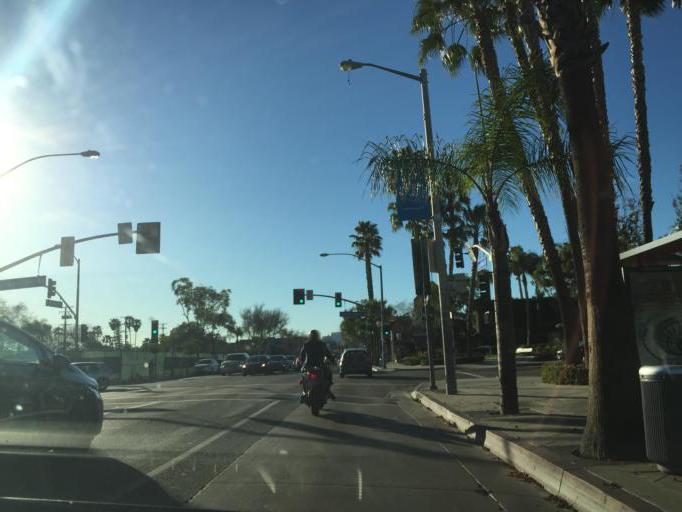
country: US
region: California
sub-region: Los Angeles County
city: West Hollywood
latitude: 34.0909
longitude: -118.3655
